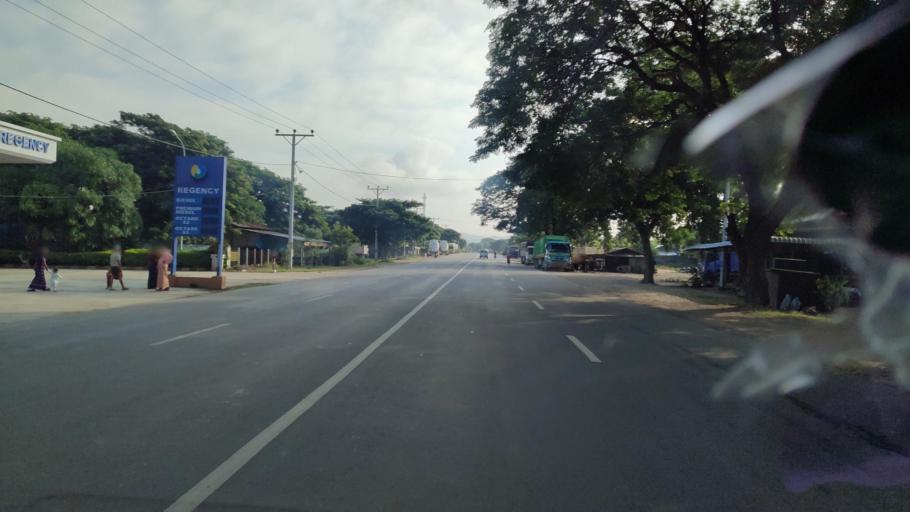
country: MM
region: Mandalay
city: Yamethin
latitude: 20.7537
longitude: 96.2475
